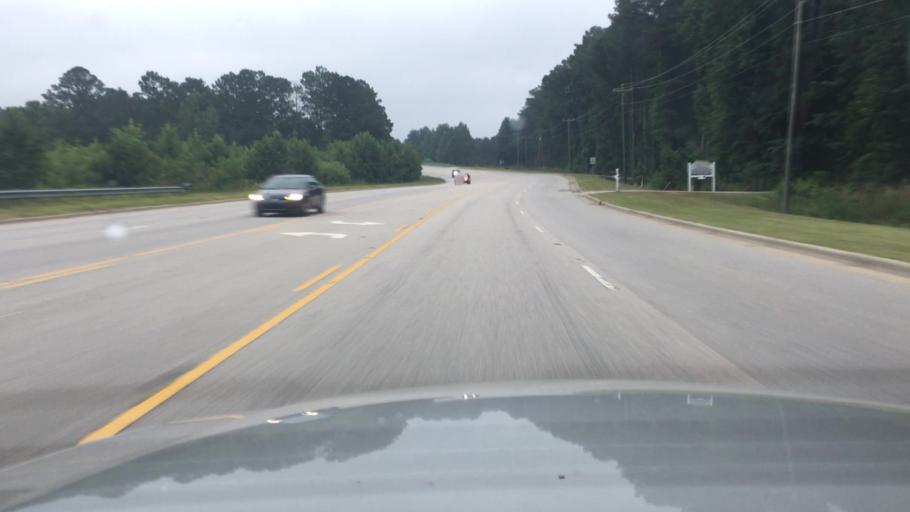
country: US
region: North Carolina
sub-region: Cumberland County
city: Fayetteville
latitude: 35.0098
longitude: -78.8749
